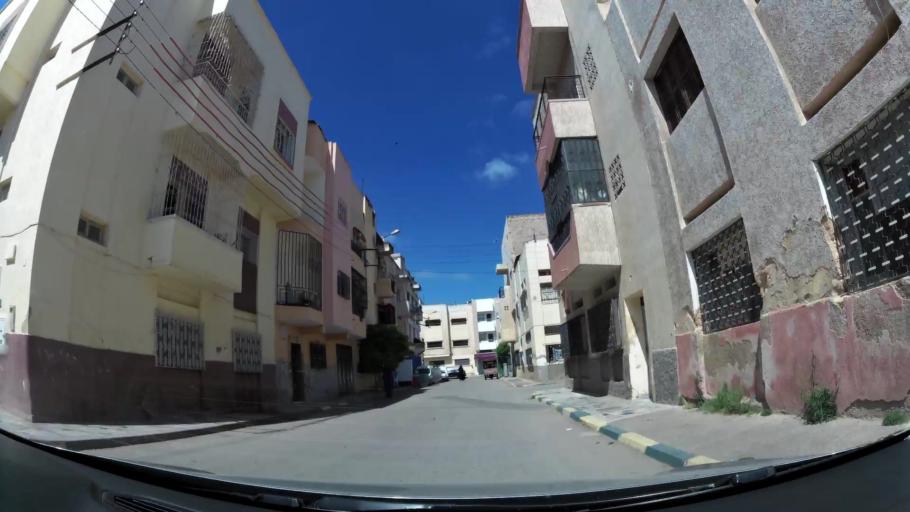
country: MA
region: Fes-Boulemane
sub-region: Fes
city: Fes
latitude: 34.0393
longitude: -5.0284
